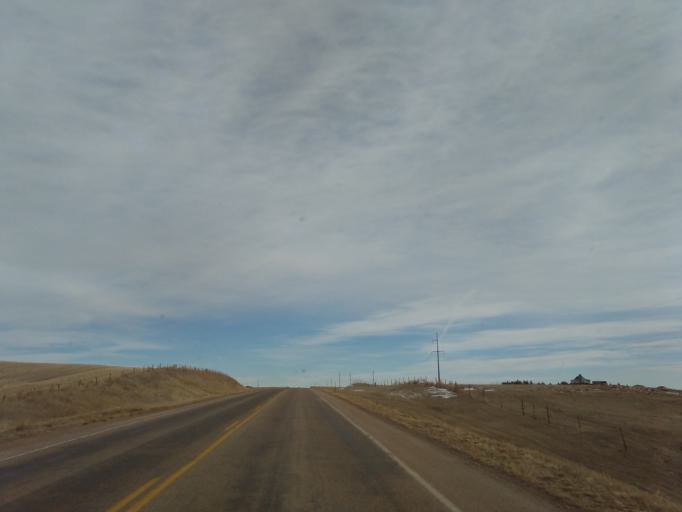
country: US
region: Wyoming
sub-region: Laramie County
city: Ranchettes
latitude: 41.3791
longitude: -104.5329
